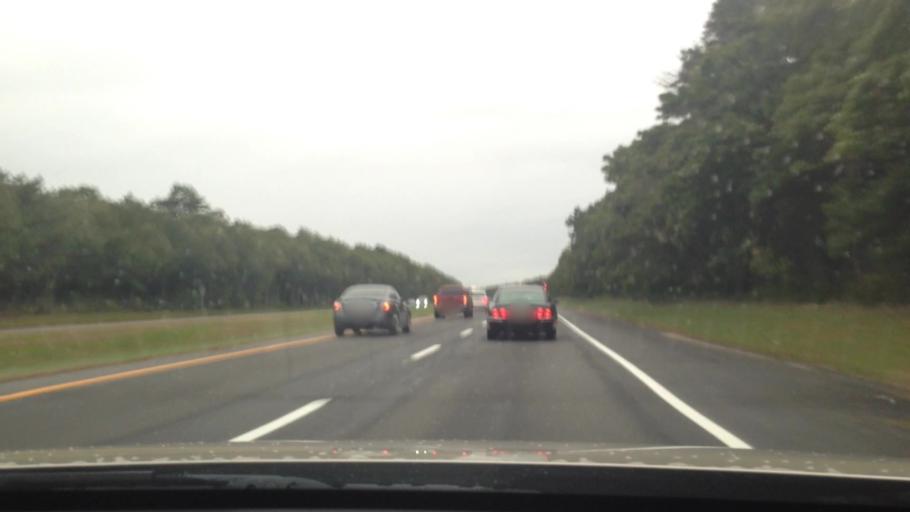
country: US
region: New York
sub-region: Suffolk County
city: Holtsville
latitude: 40.7981
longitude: -73.0514
